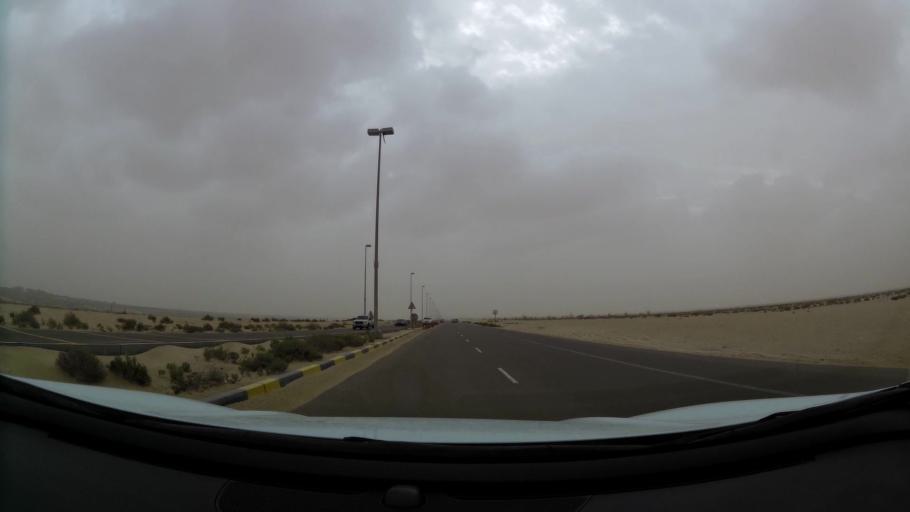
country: AE
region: Abu Dhabi
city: Abu Dhabi
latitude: 24.4613
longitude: 54.6915
